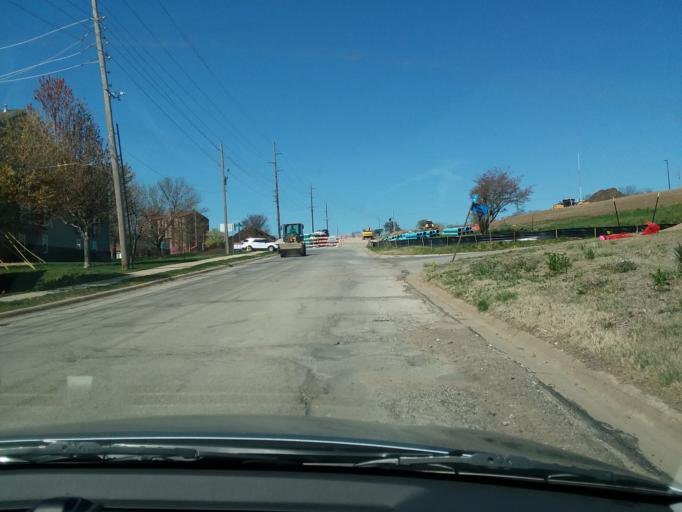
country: US
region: Kansas
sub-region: Douglas County
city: Lawrence
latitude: 38.9501
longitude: -95.2579
